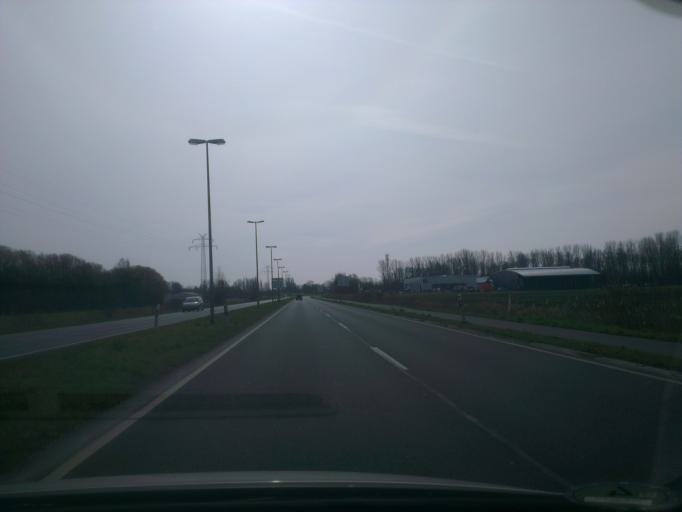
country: DE
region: Lower Saxony
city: Emden
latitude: 53.3615
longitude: 7.1735
